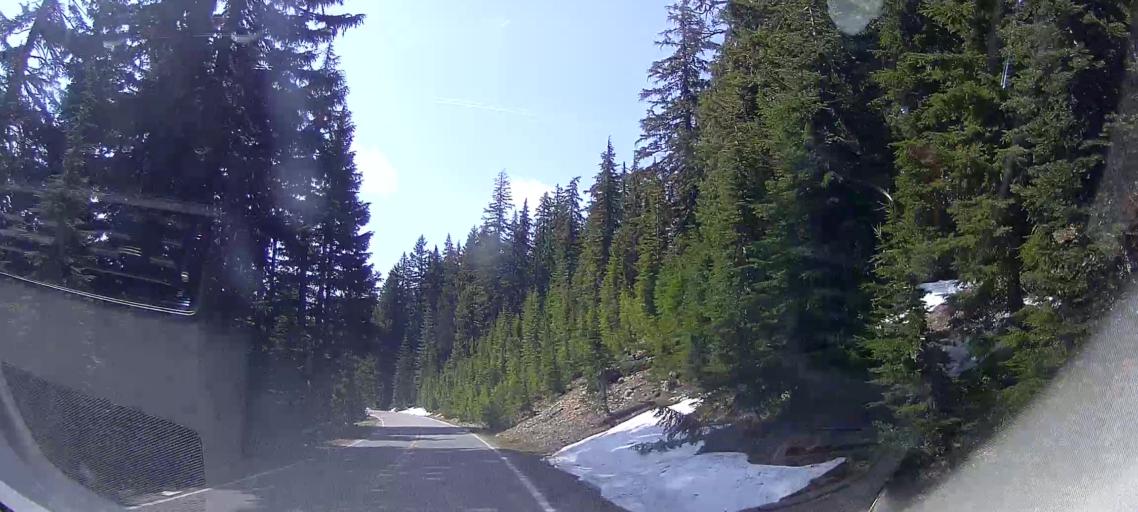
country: US
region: Oregon
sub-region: Klamath County
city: Klamath Falls
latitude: 42.8943
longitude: -122.0996
